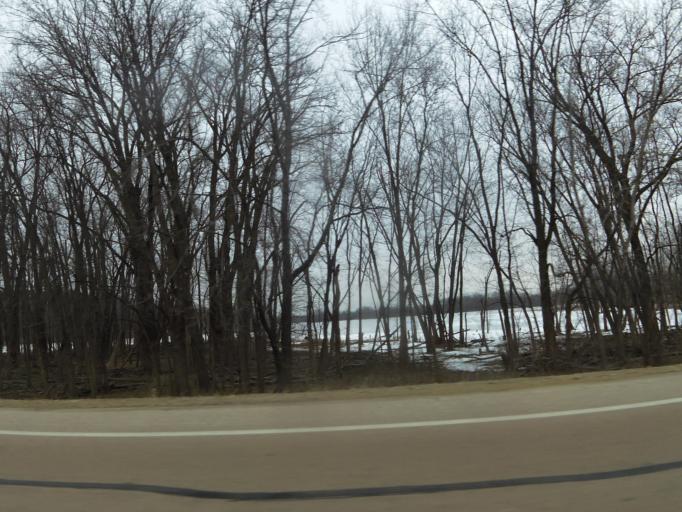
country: US
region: Minnesota
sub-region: Scott County
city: Jordan
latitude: 44.7027
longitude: -93.6454
